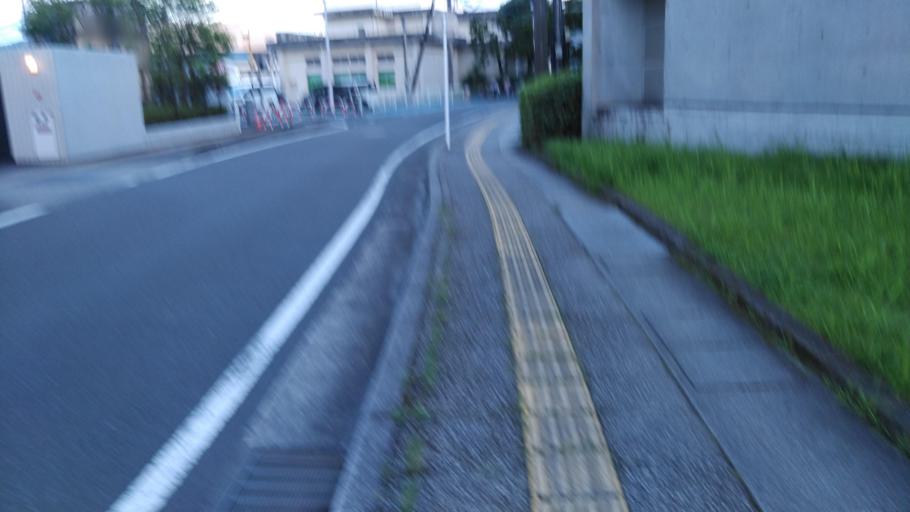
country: JP
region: Kagoshima
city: Kokubu-matsuki
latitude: 31.7410
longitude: 130.7637
